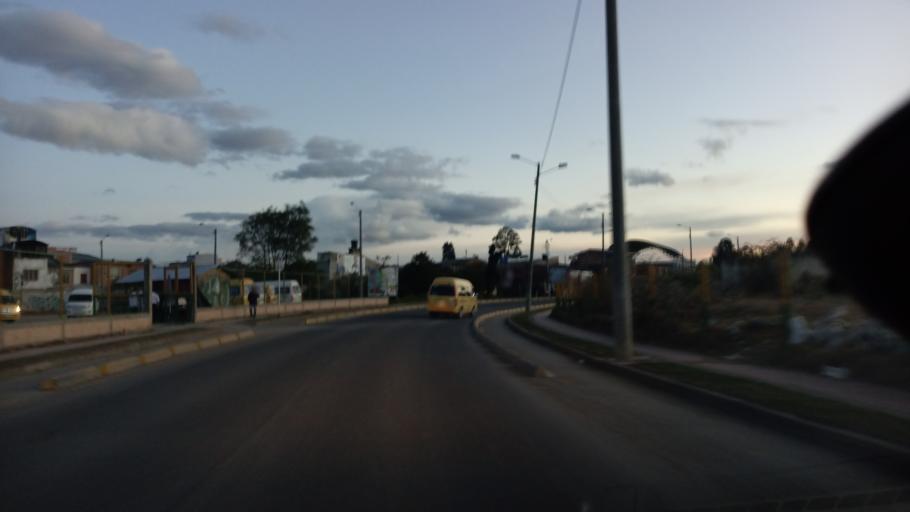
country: CO
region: Cundinamarca
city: Chia
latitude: 4.8587
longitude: -74.0665
